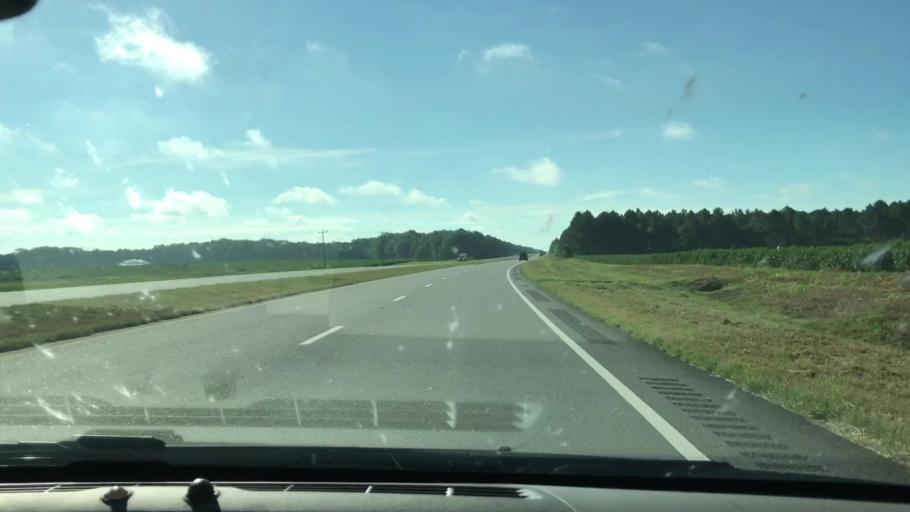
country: US
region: Georgia
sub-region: Terrell County
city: Dawson
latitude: 31.6979
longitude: -84.3211
